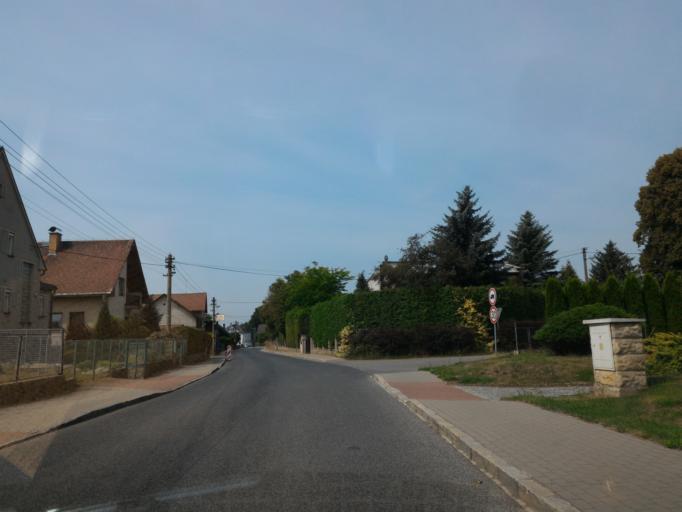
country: CZ
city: Prisovice
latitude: 50.5799
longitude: 15.0925
